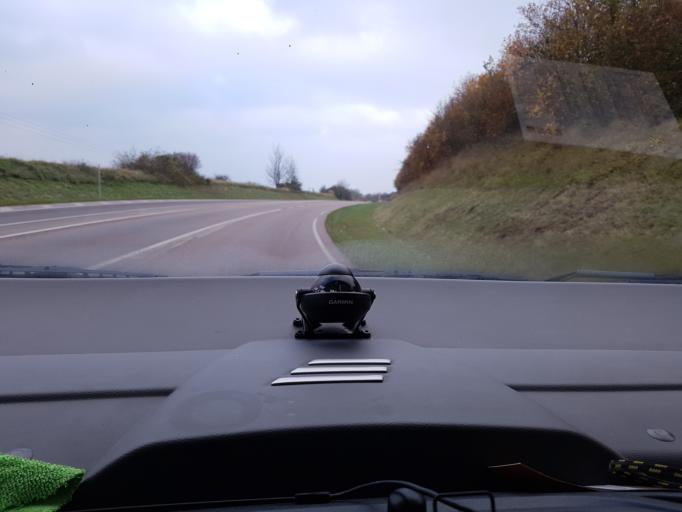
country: FR
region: Haute-Normandie
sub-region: Departement de la Seine-Maritime
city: Eu
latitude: 50.0598
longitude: 1.4183
